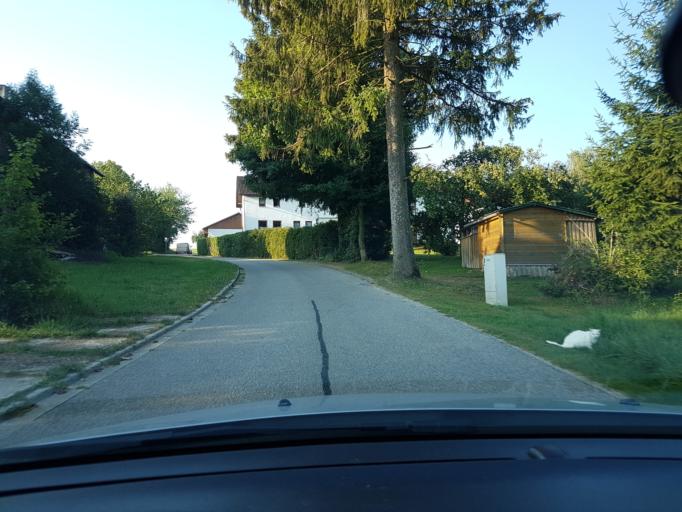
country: DE
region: Bavaria
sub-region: Upper Bavaria
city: Egglkofen
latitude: 48.4440
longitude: 12.4747
